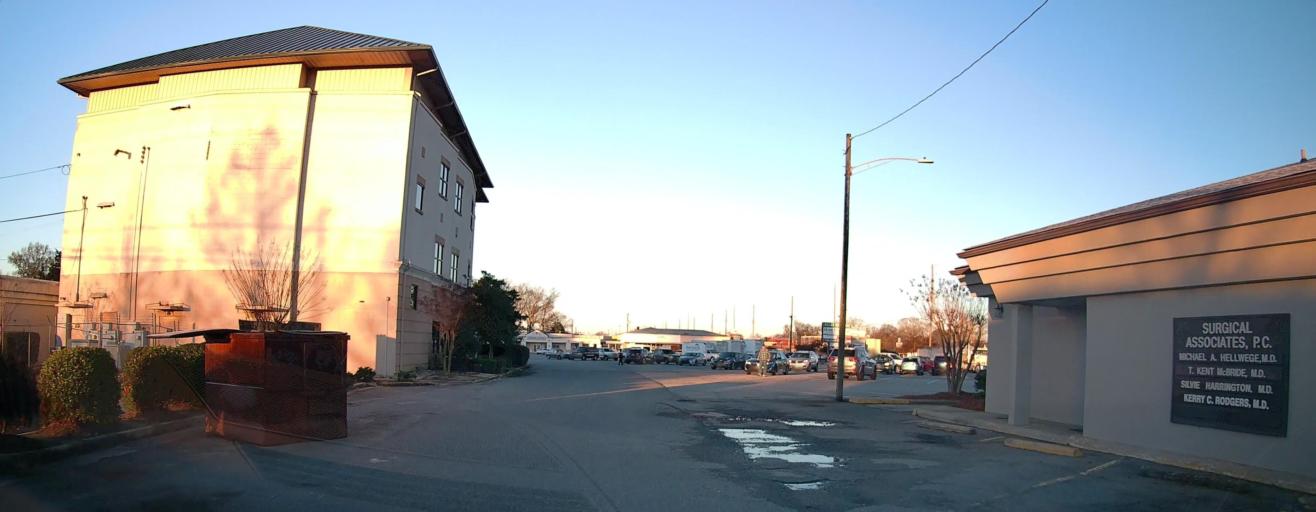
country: US
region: Georgia
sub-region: Houston County
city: Warner Robins
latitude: 32.6177
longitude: -83.6332
